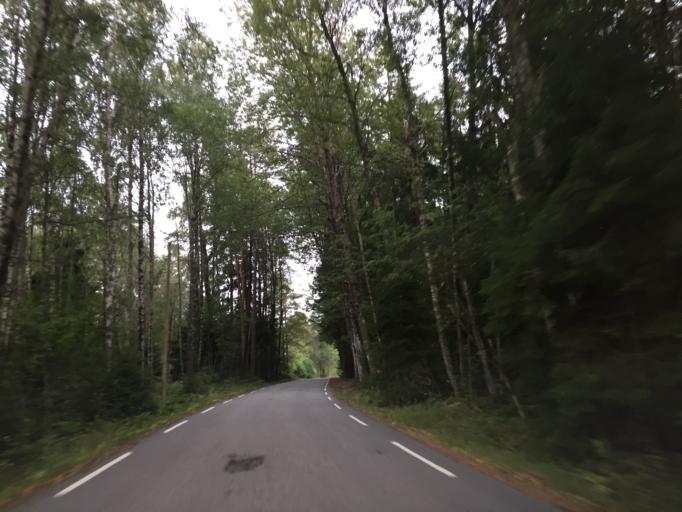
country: NO
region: Ostfold
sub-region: Hvaler
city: Skjaerhalden
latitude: 59.0625
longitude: 11.0070
